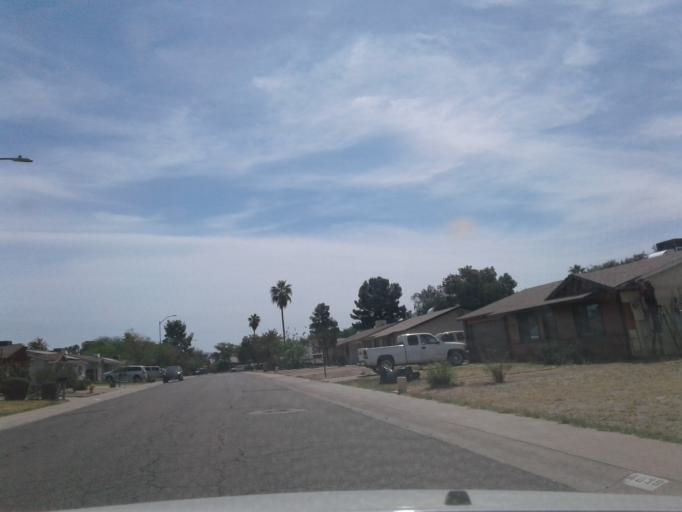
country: US
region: Arizona
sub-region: Maricopa County
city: Paradise Valley
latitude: 33.6140
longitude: -111.9943
